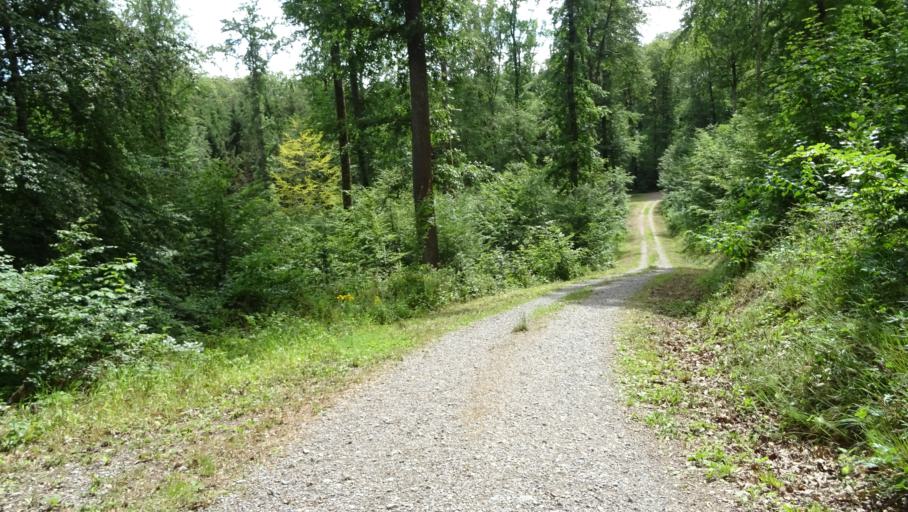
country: DE
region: Baden-Wuerttemberg
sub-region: Karlsruhe Region
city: Obrigheim
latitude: 49.3832
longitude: 9.1145
